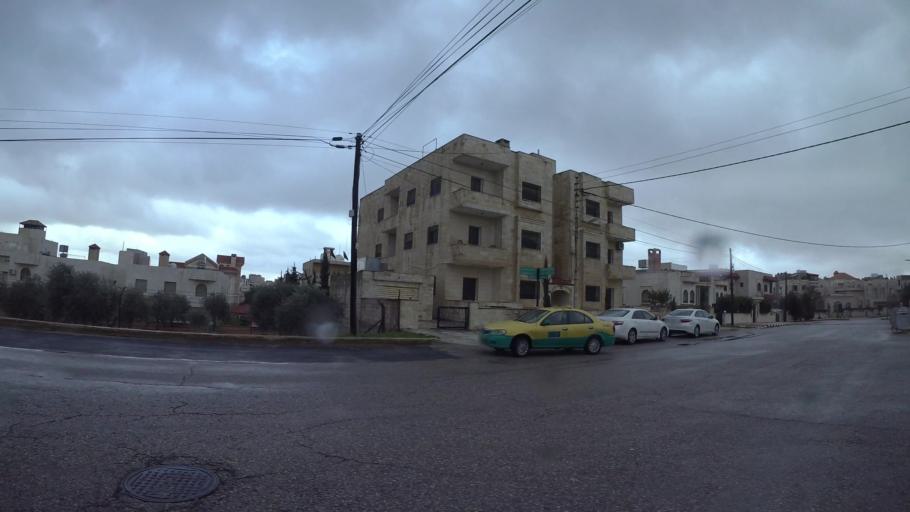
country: JO
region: Amman
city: Al Jubayhah
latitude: 32.0343
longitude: 35.8607
